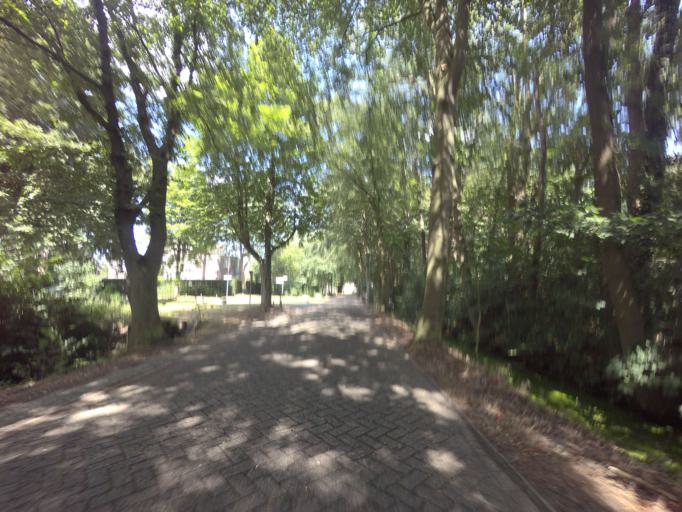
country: NL
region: Utrecht
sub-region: Gemeente Zeist
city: Zeist
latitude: 52.0765
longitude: 5.2396
